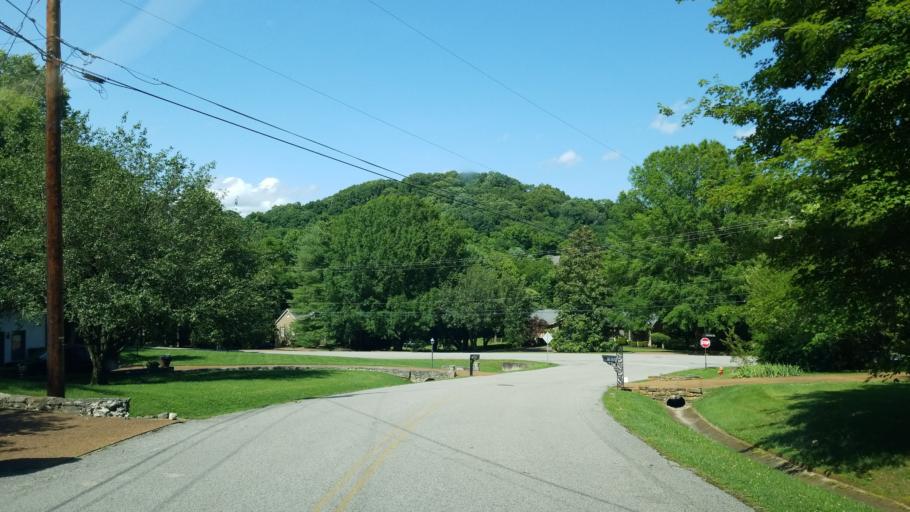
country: US
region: Tennessee
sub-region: Williamson County
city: Brentwood
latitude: 36.0477
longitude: -86.7933
